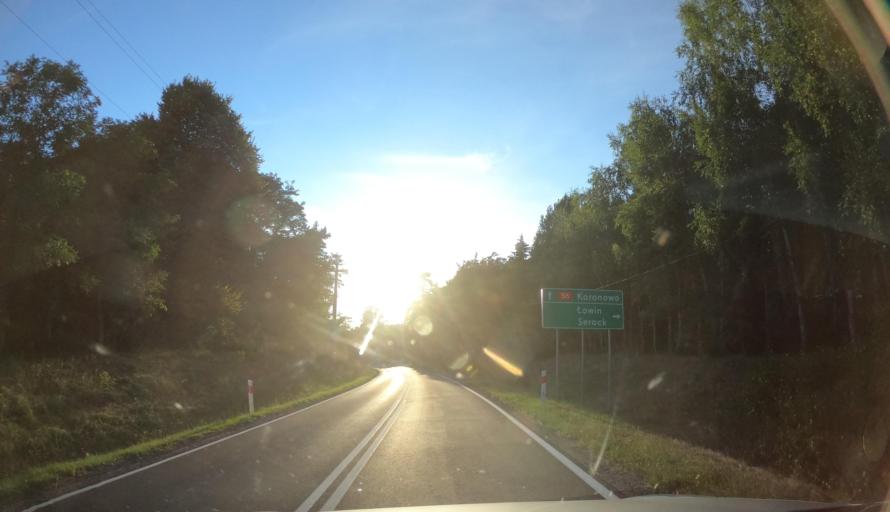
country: PL
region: Kujawsko-Pomorskie
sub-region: Powiat bydgoski
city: Koronowo
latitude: 53.3138
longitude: 17.9886
